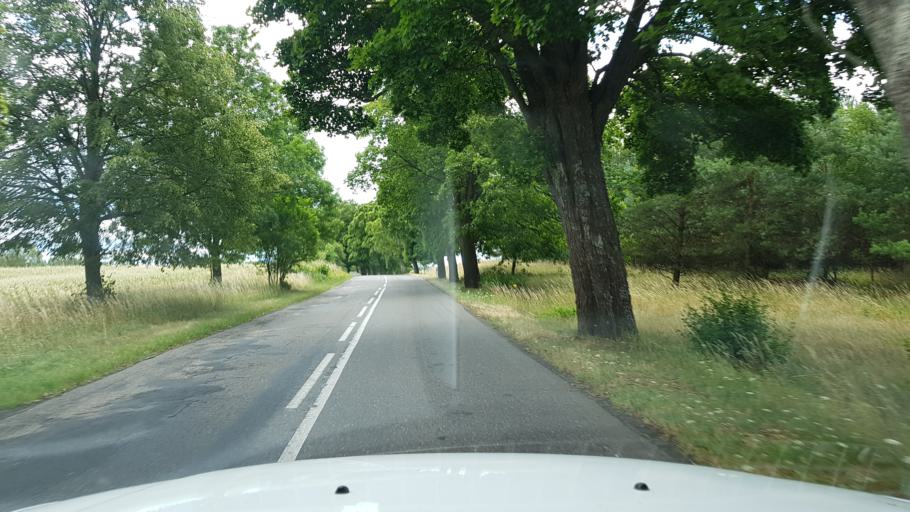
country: PL
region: West Pomeranian Voivodeship
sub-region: Powiat stargardzki
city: Insko
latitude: 53.3869
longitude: 15.5766
